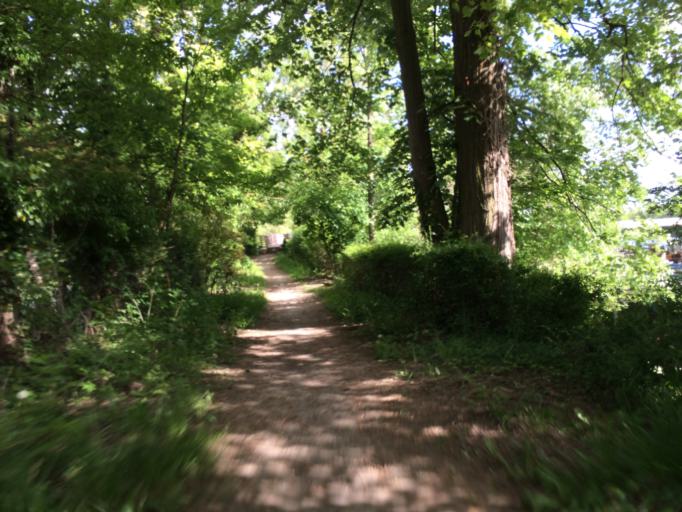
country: FR
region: Ile-de-France
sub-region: Departement de l'Essonne
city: Viry-Chatillon
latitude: 48.6747
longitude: 2.3963
